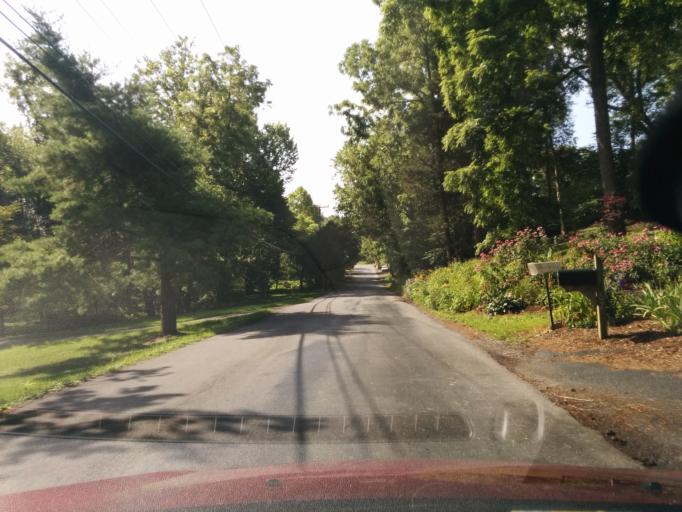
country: US
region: Virginia
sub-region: City of Lexington
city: Lexington
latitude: 37.7677
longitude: -79.4590
